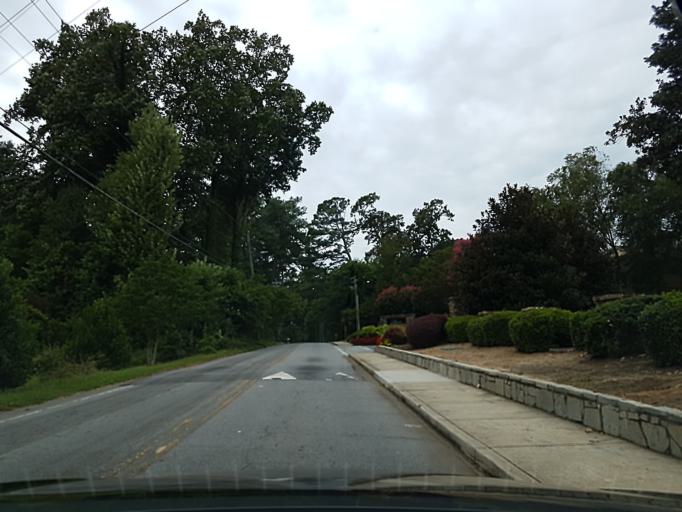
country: US
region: Georgia
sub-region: DeKalb County
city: North Druid Hills
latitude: 33.8248
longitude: -84.3395
